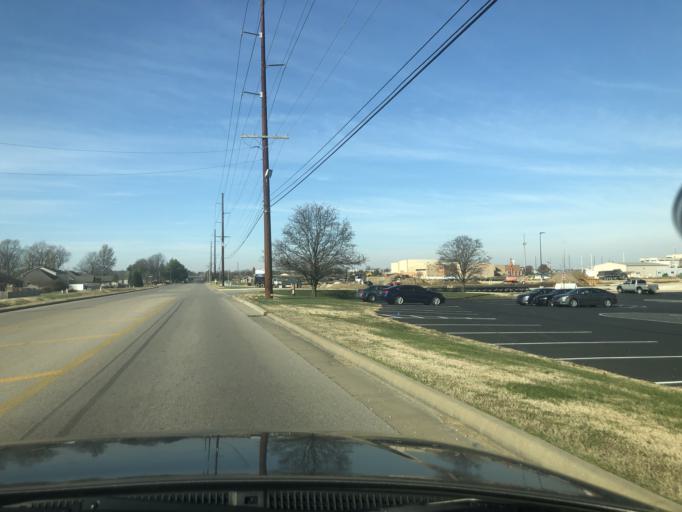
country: US
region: Indiana
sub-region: Warrick County
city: Newburgh
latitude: 37.9695
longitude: -87.4421
